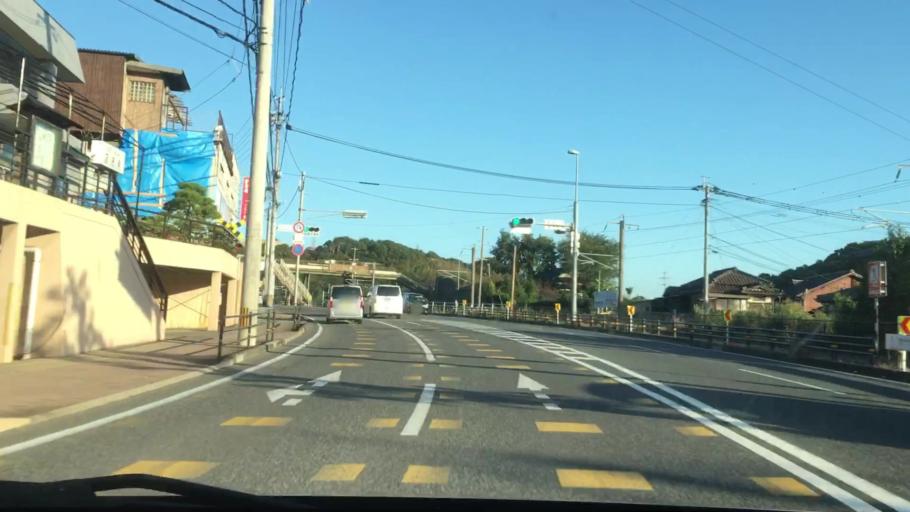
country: JP
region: Nagasaki
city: Sasebo
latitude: 33.1564
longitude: 129.7531
